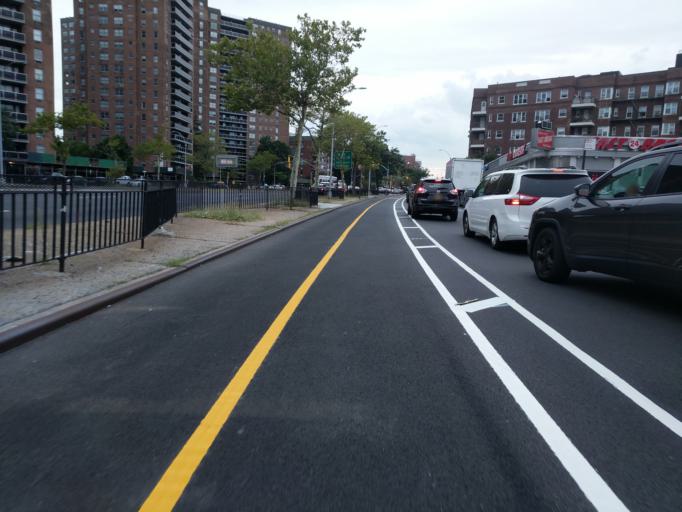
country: US
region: New York
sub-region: Queens County
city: Borough of Queens
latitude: 40.7235
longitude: -73.8481
